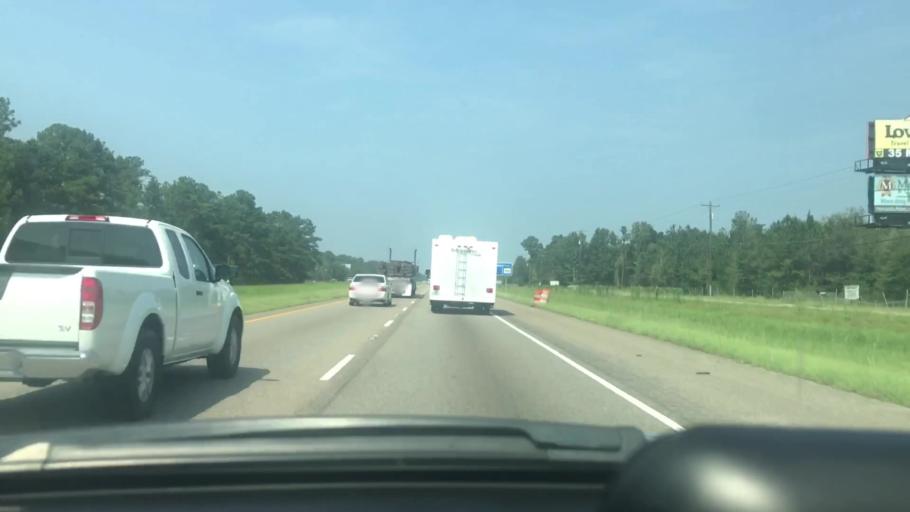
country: US
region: Louisiana
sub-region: Livingston Parish
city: Albany
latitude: 30.4749
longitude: -90.6237
